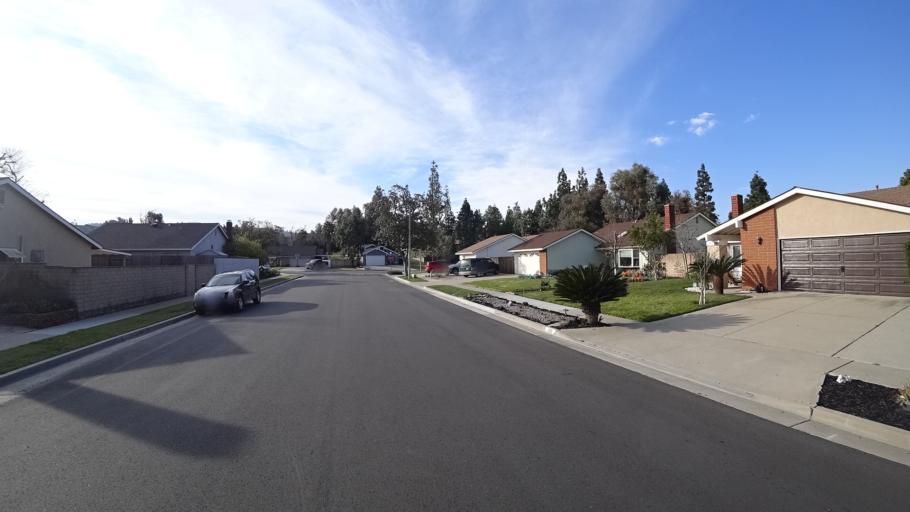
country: US
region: California
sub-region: Orange County
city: Yorba Linda
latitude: 33.8536
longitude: -117.8144
